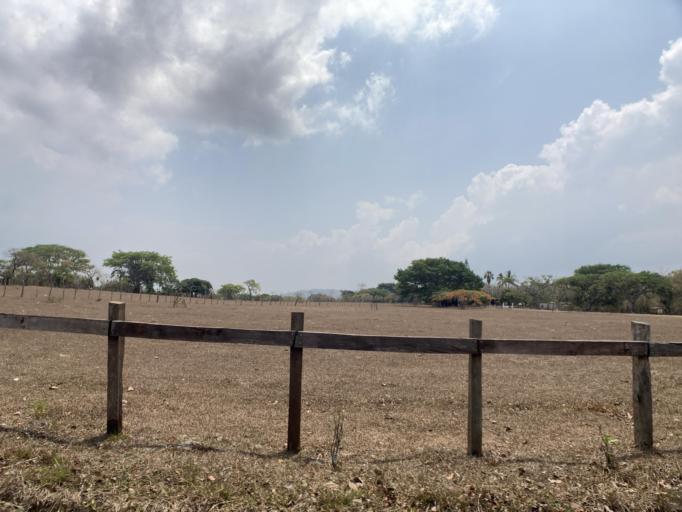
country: GT
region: Santa Rosa
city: Pueblo Nuevo Vinas
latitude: 14.3223
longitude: -90.5267
